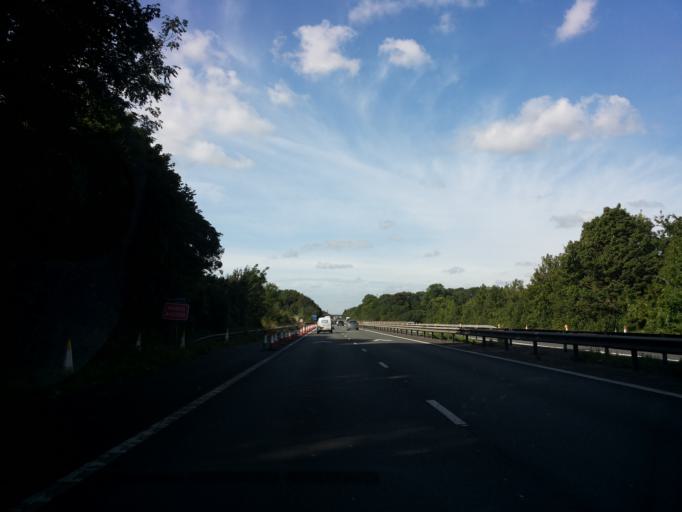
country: GB
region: England
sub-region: Kent
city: Sittingbourne
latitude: 51.3018
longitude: 0.7289
